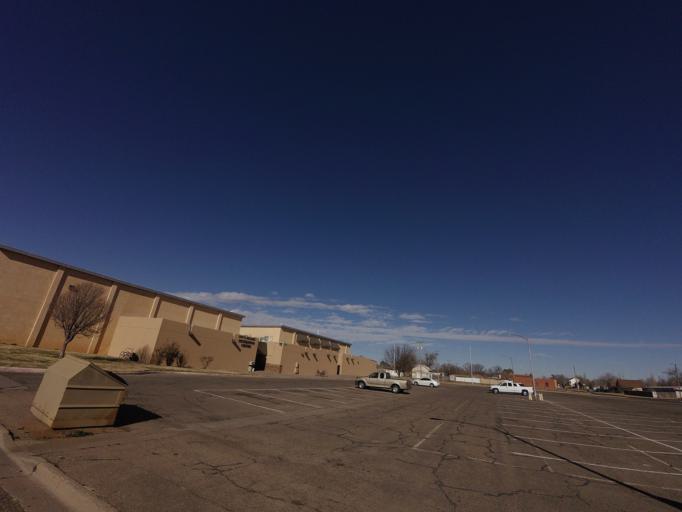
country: US
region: New Mexico
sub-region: Curry County
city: Clovis
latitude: 34.3997
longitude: -103.2096
